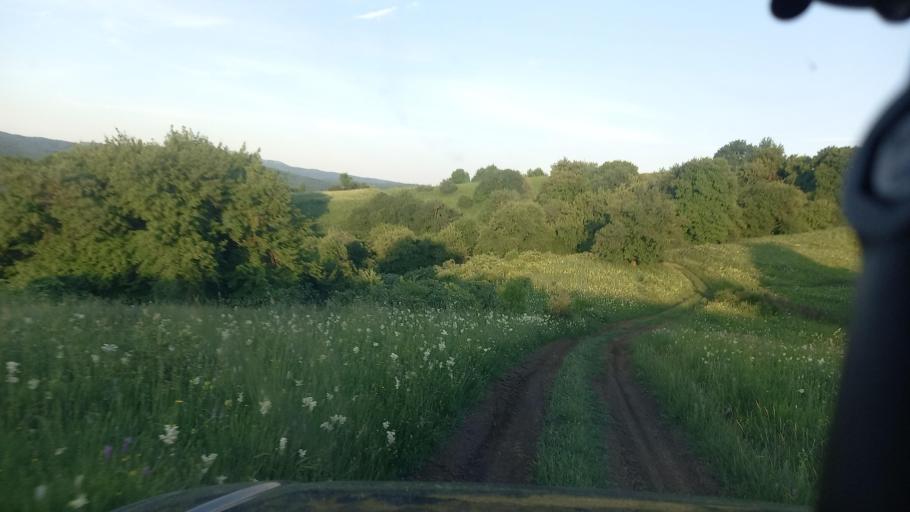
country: RU
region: Karachayevo-Cherkesiya
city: Kurdzhinovo
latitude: 44.1242
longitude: 41.0911
